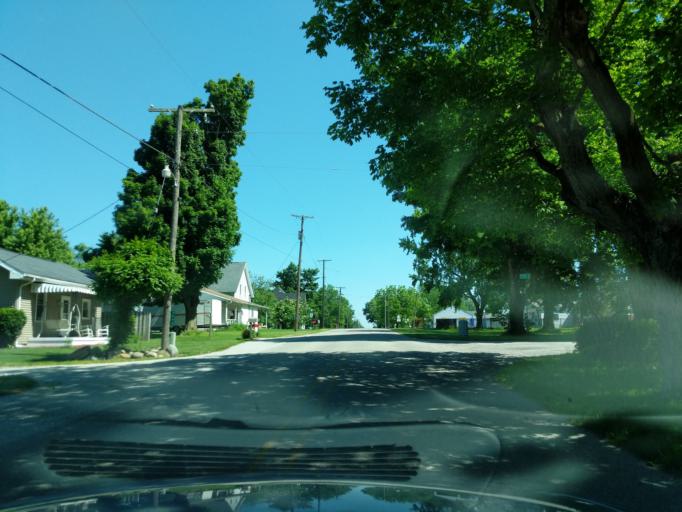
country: US
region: Indiana
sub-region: Huntington County
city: Warren
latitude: 40.7487
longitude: -85.5070
